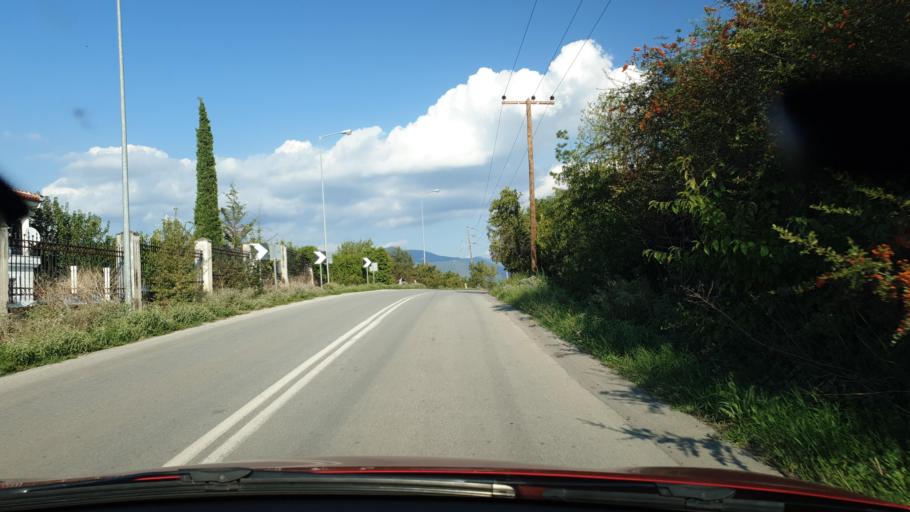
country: GR
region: Central Macedonia
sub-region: Nomos Thessalonikis
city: Agia Paraskevi
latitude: 40.4832
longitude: 23.0556
